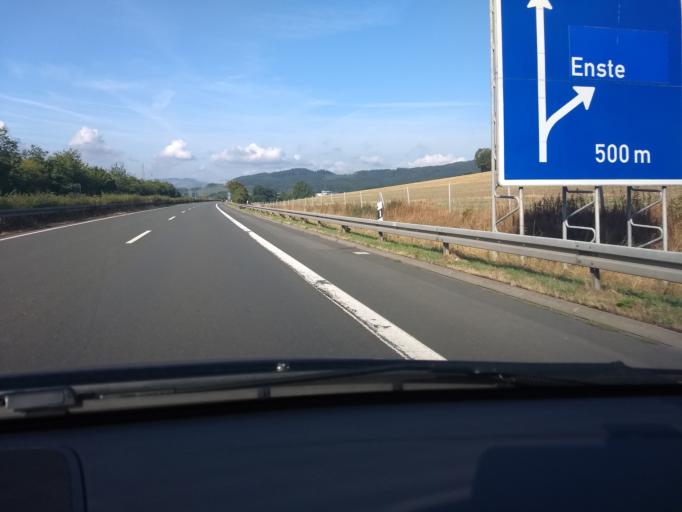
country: DE
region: North Rhine-Westphalia
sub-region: Regierungsbezirk Arnsberg
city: Meschede
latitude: 51.3607
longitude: 8.2621
